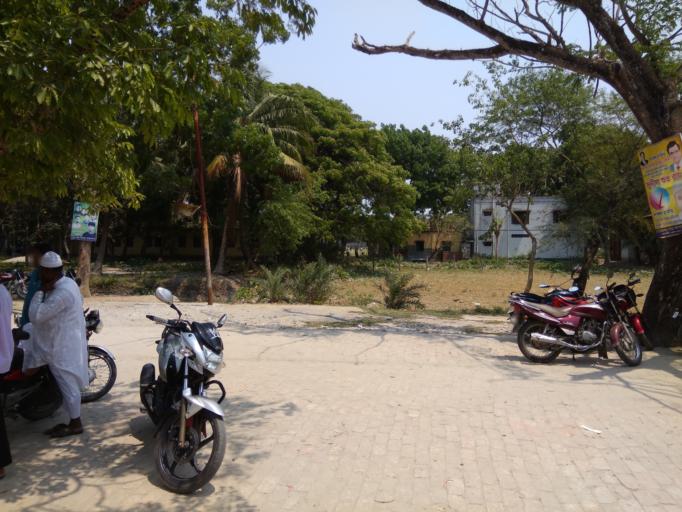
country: BD
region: Khulna
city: Phultala
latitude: 22.7362
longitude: 89.5153
